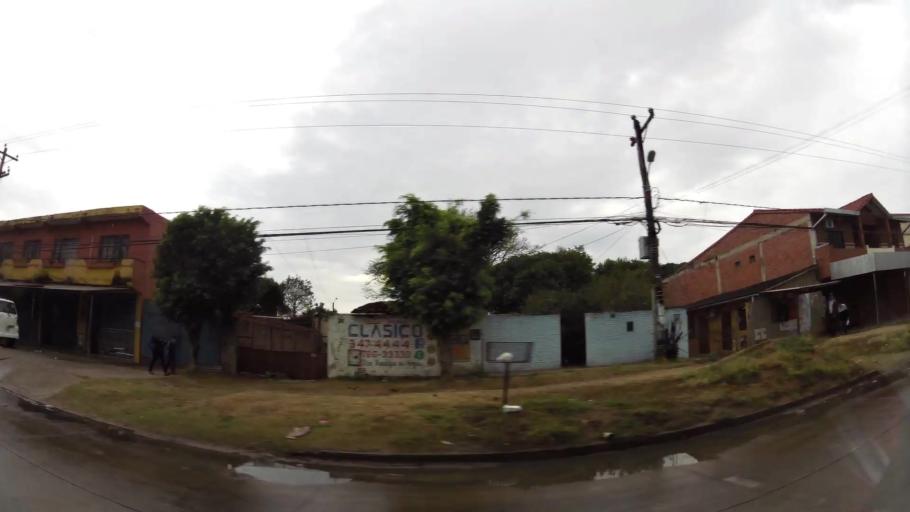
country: BO
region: Santa Cruz
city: Santa Cruz de la Sierra
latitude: -17.7807
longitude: -63.1421
